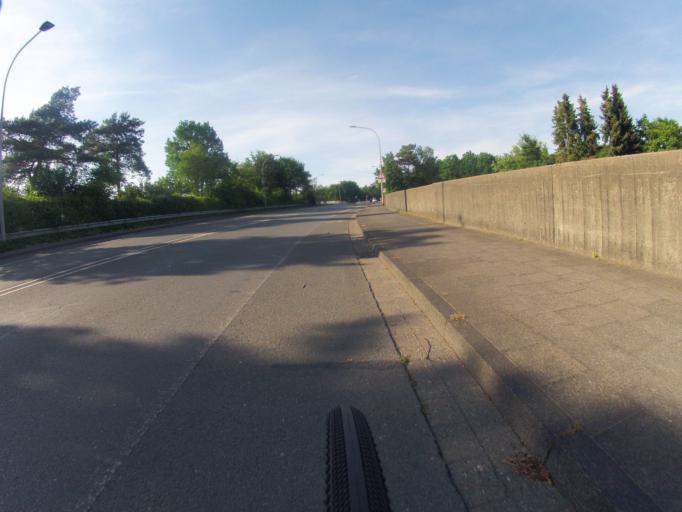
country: DE
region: North Rhine-Westphalia
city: Ibbenburen
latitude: 52.2811
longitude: 7.7123
